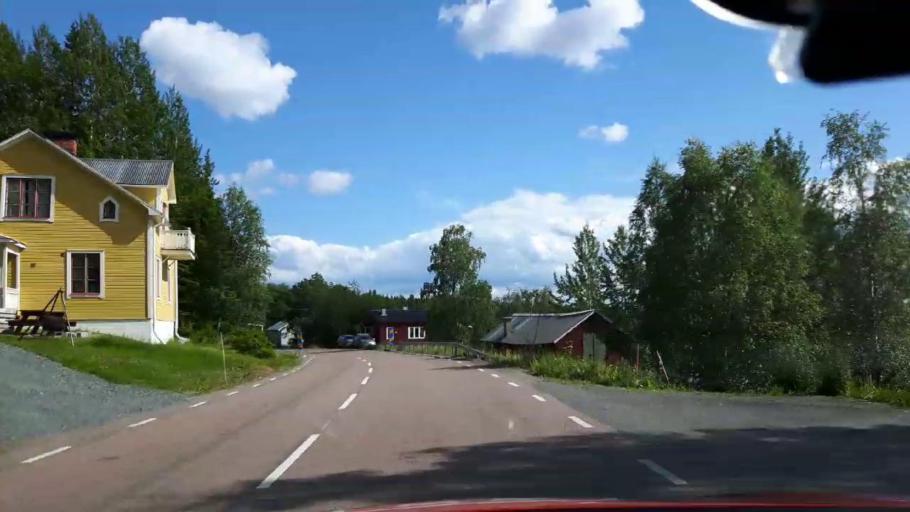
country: SE
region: Jaemtland
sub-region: Krokoms Kommun
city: Valla
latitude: 64.0668
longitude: 14.1414
